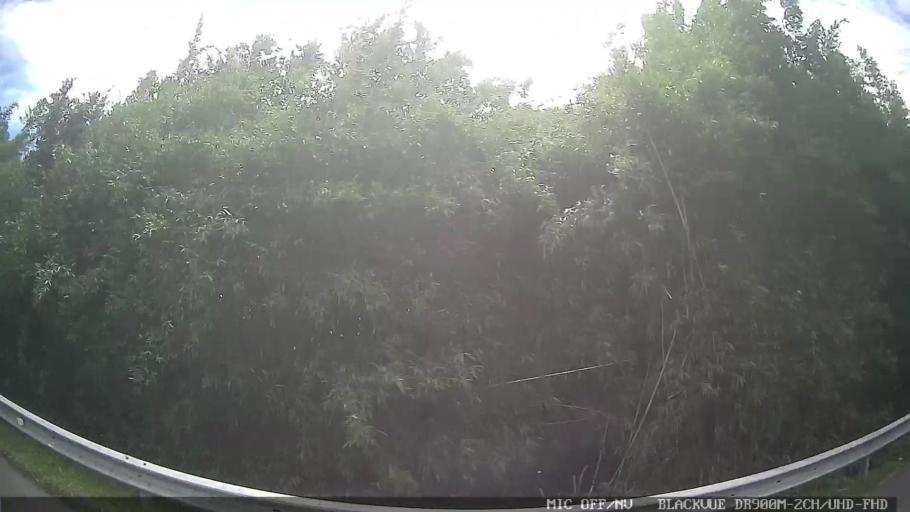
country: BR
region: Sao Paulo
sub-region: Laranjal Paulista
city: Laranjal Paulista
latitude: -23.0571
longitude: -47.8233
